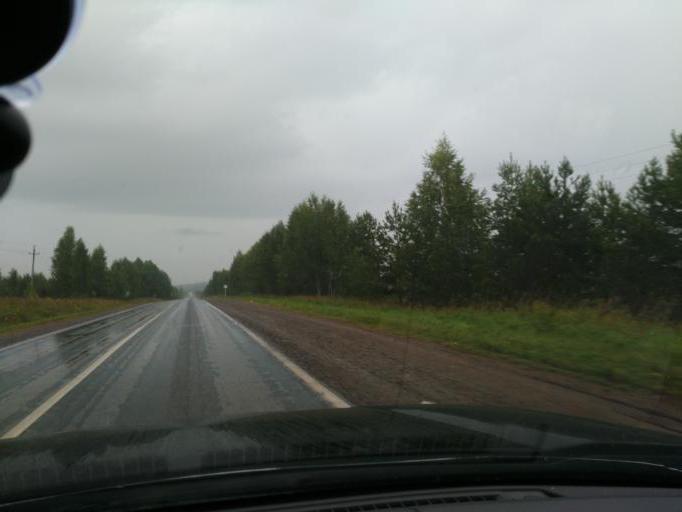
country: RU
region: Perm
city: Osa
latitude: 57.1271
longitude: 55.5248
